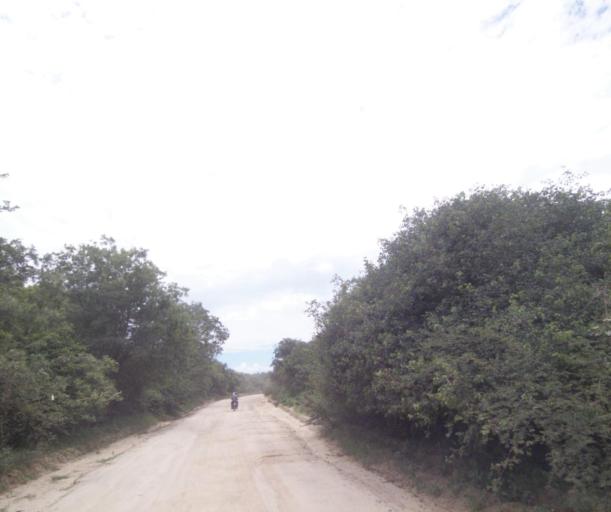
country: BR
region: Bahia
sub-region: Carinhanha
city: Carinhanha
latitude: -14.2118
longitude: -43.8998
